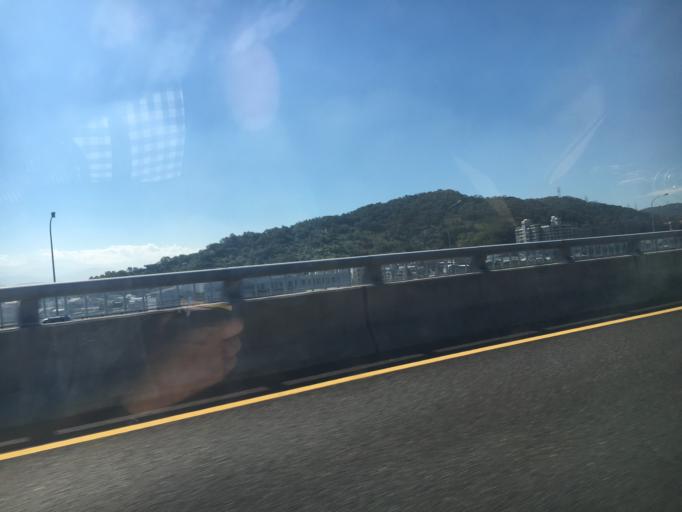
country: TW
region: Taipei
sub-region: Taipei
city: Banqiao
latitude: 25.0687
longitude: 121.4317
